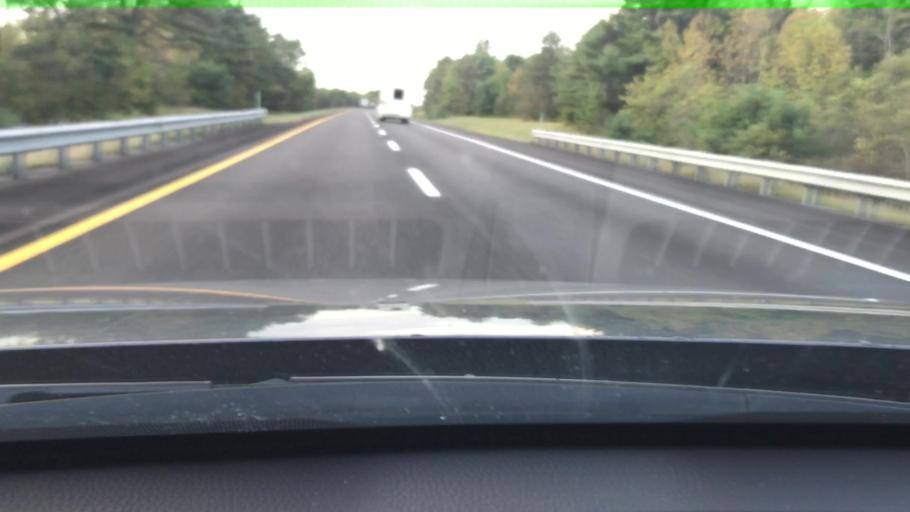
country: US
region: Maine
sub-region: Sagadahoc County
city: Richmond
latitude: 44.0703
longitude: -69.8813
